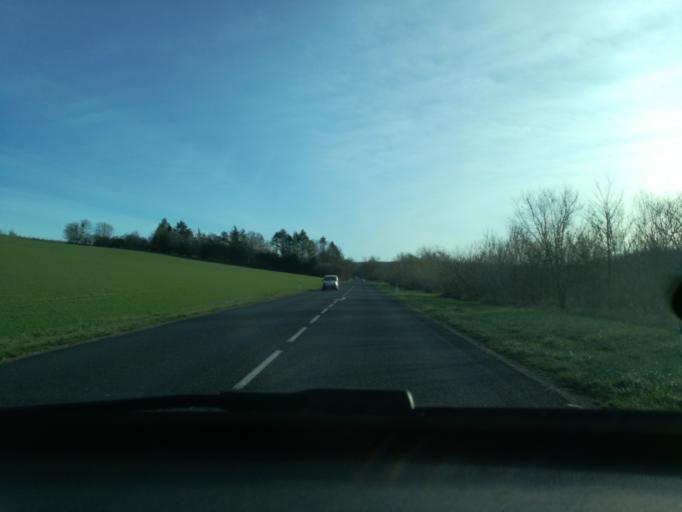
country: FR
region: Lorraine
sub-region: Departement de la Meuse
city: Fains-Veel
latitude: 48.8028
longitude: 5.1170
